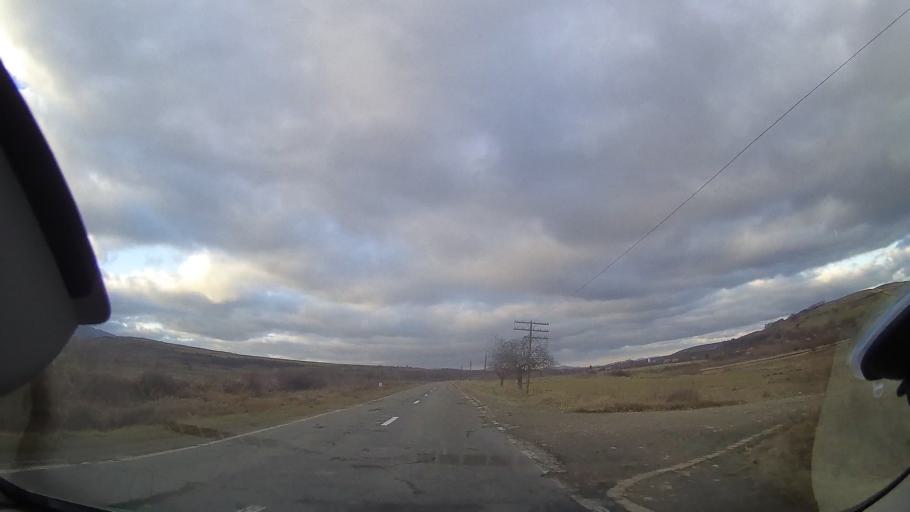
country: RO
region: Cluj
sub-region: Comuna Calatele
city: Calatele
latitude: 46.7905
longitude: 22.9981
